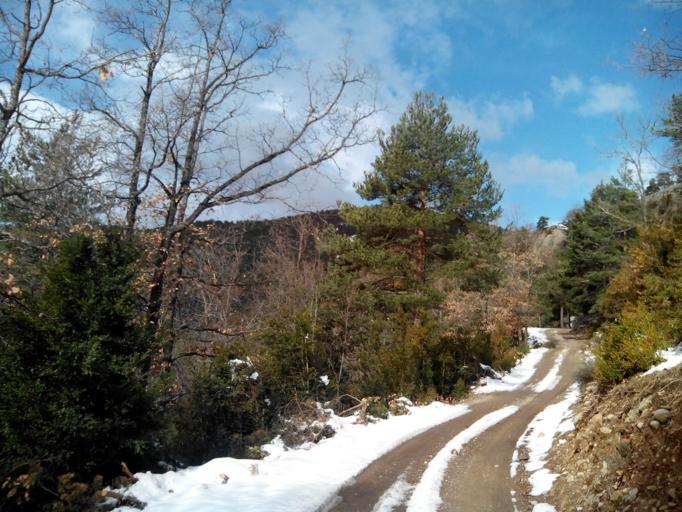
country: ES
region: Catalonia
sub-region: Provincia de Barcelona
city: Vilada
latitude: 42.1858
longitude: 1.9309
